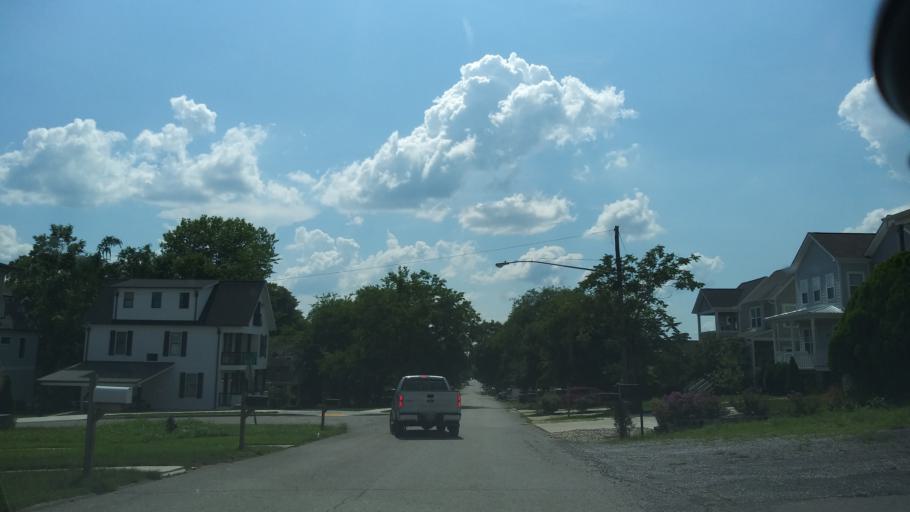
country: US
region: Tennessee
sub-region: Davidson County
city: Nashville
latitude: 36.1589
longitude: -86.8434
